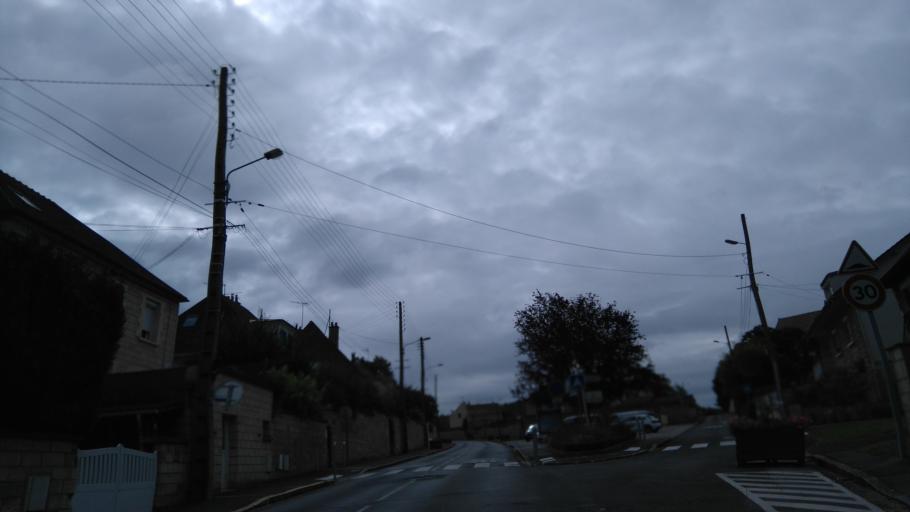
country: FR
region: Picardie
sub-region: Departement de l'Oise
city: Saint-Maximin
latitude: 49.2219
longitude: 2.4449
